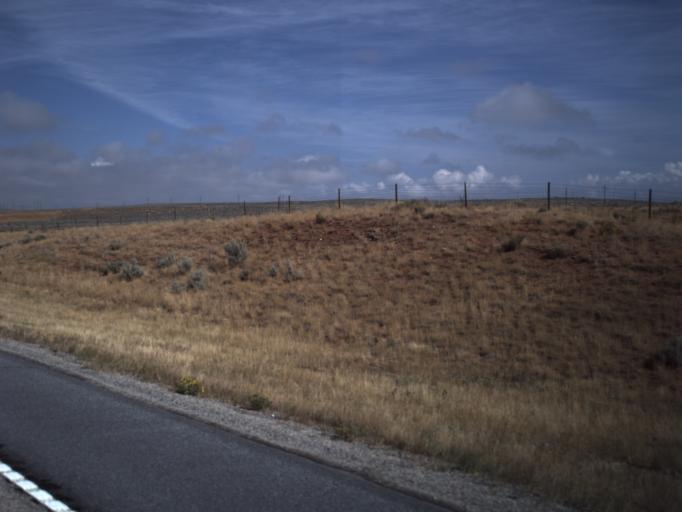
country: US
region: Wyoming
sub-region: Uinta County
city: Evanston
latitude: 41.4128
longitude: -111.0453
